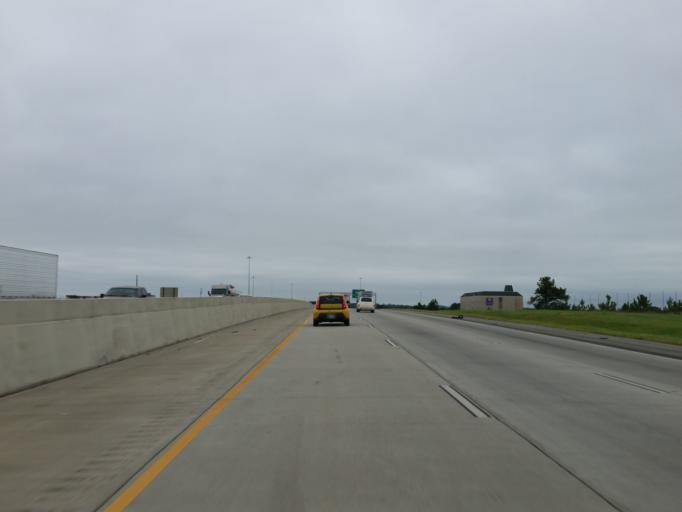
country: US
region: Georgia
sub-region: Crisp County
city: Cordele
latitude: 31.9413
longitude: -83.7486
